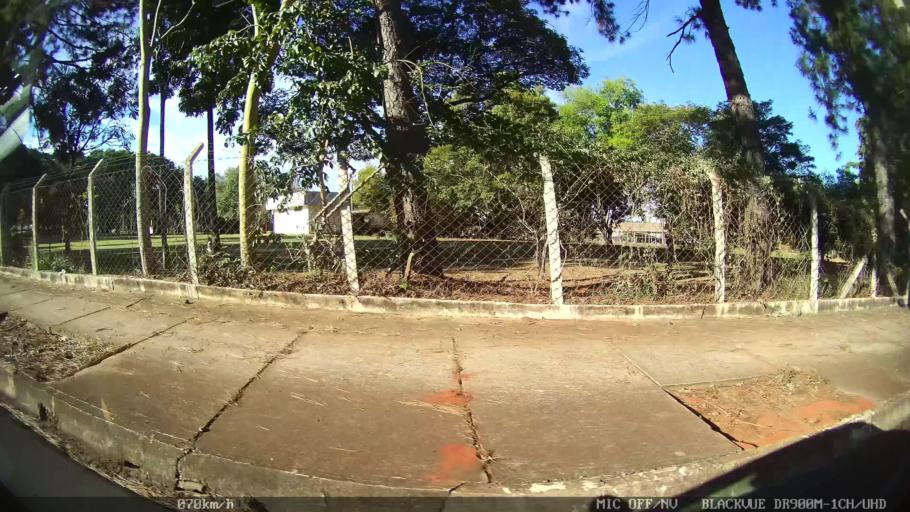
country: BR
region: Sao Paulo
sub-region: Araraquara
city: Araraquara
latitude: -21.7537
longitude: -48.1818
